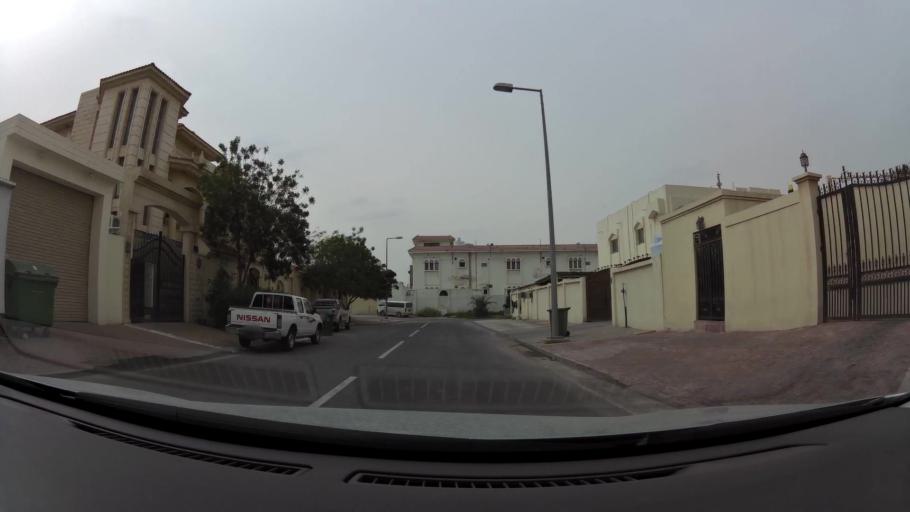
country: QA
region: Baladiyat ad Dawhah
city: Doha
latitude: 25.2489
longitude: 51.5126
